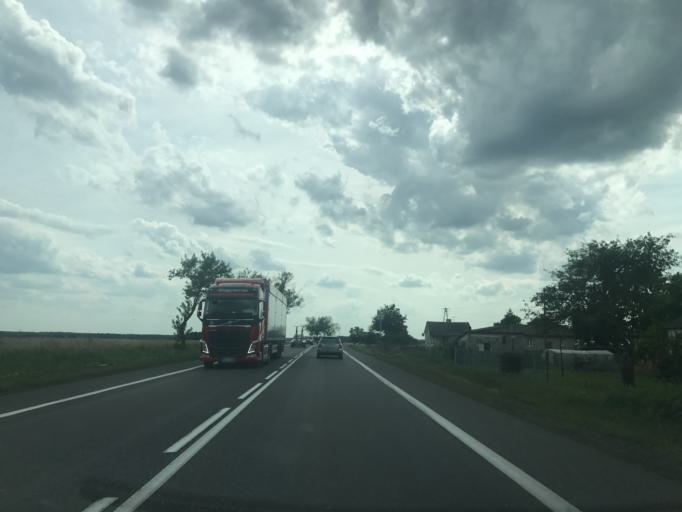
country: PL
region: Masovian Voivodeship
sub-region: Powiat mlawski
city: Strzegowo
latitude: 52.9582
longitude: 20.2989
